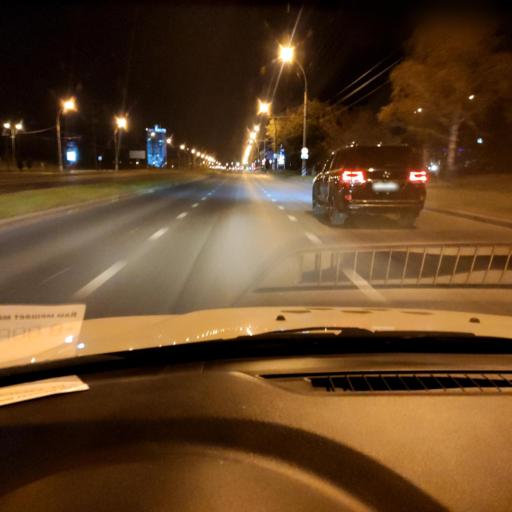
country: RU
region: Samara
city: Tol'yatti
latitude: 53.5444
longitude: 49.2650
